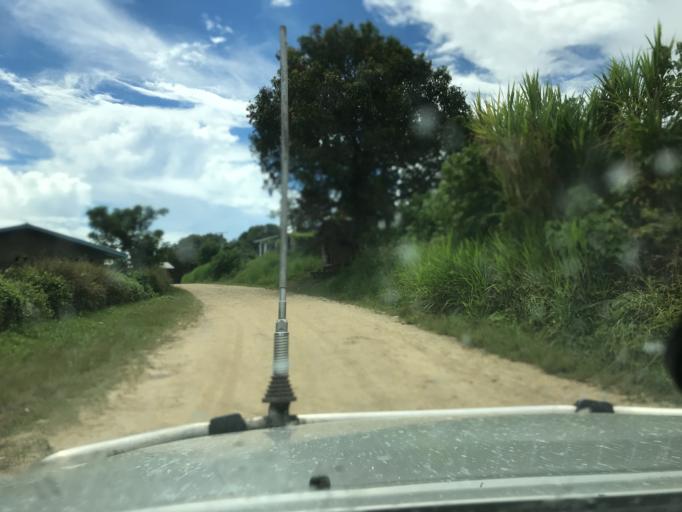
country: SB
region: Malaita
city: Auki
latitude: -8.3530
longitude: 160.6333
